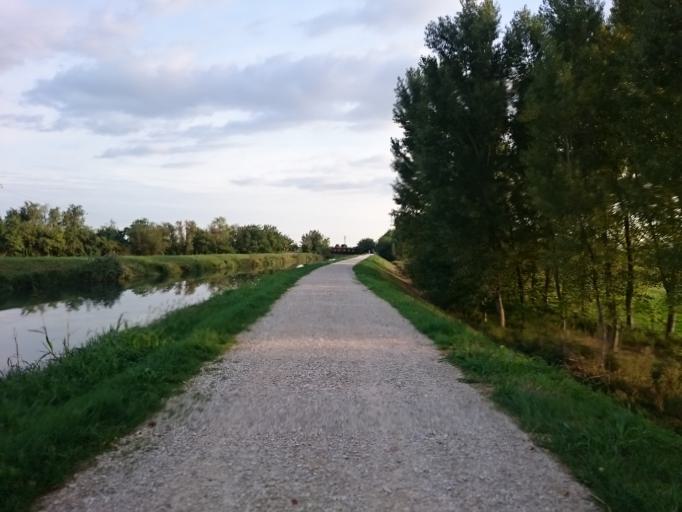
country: IT
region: Veneto
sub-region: Provincia di Padova
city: Campodoro
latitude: 45.4939
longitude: 11.7331
